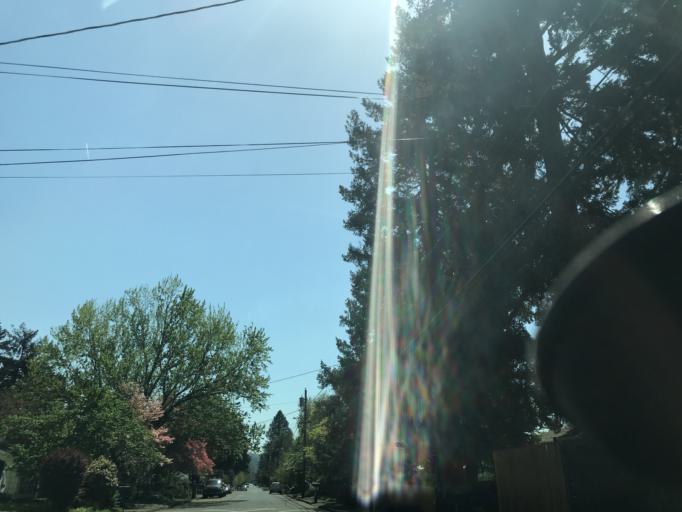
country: US
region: Oregon
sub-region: Multnomah County
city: Lents
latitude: 45.4929
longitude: -122.5609
